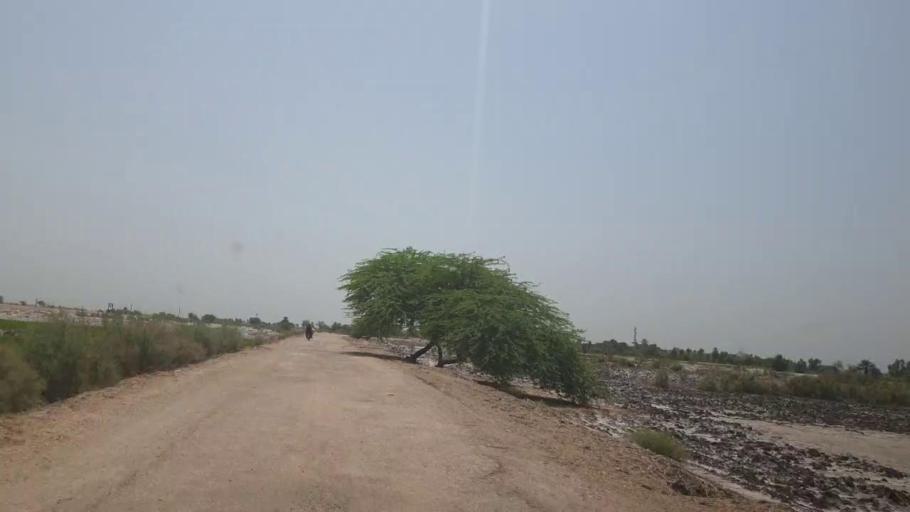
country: PK
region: Sindh
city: Lakhi
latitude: 27.8648
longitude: 68.6627
